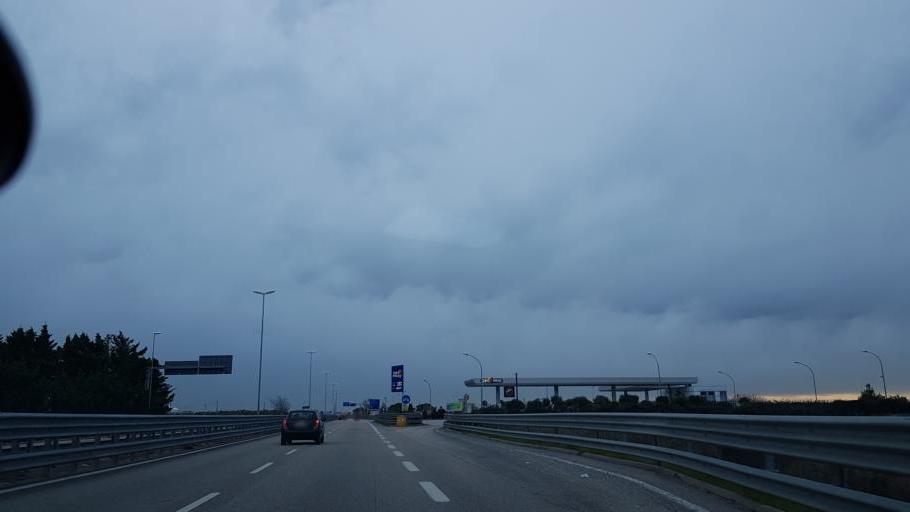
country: IT
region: Apulia
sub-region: Provincia di Brindisi
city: Brindisi
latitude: 40.6216
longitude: 17.9117
